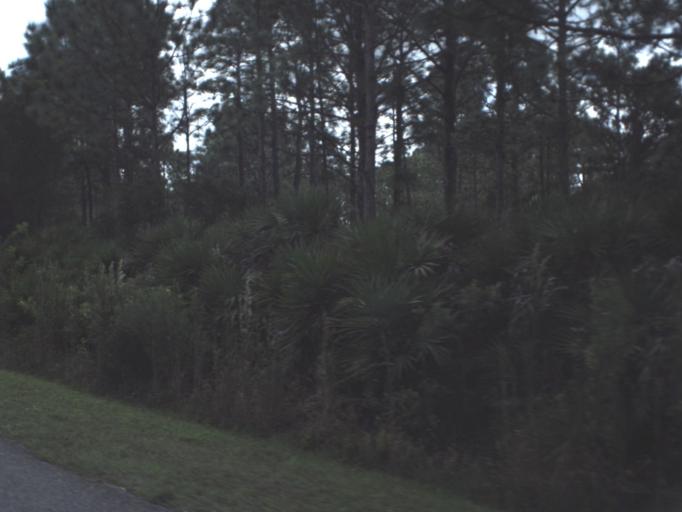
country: US
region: Florida
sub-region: Sarasota County
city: Fruitville
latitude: 27.3959
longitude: -82.2979
